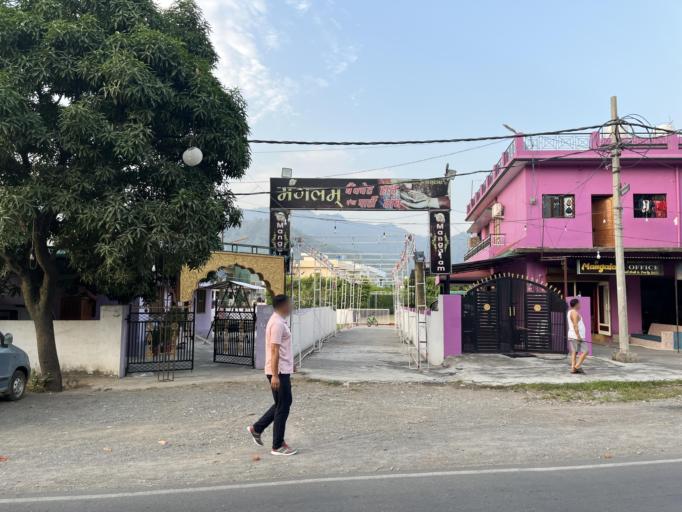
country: IN
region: Uttarakhand
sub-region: Naini Tal
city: Haldwani
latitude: 29.2369
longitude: 79.4751
